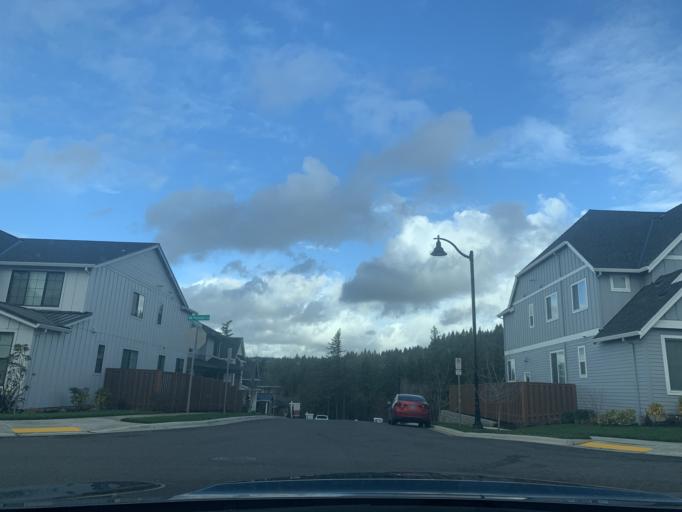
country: US
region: Oregon
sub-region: Washington County
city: Cedar Mill
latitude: 45.5512
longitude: -122.8041
